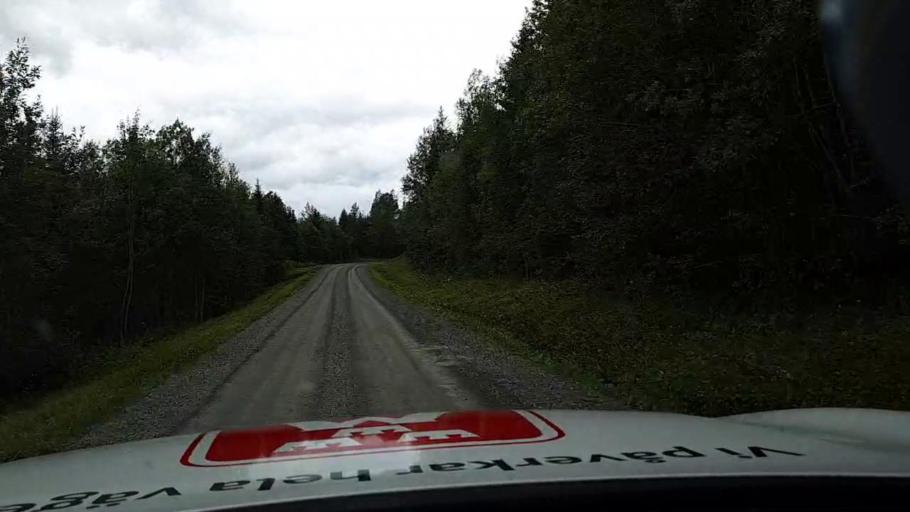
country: SE
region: Jaemtland
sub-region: Krokoms Kommun
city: Valla
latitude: 63.5243
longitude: 13.8988
